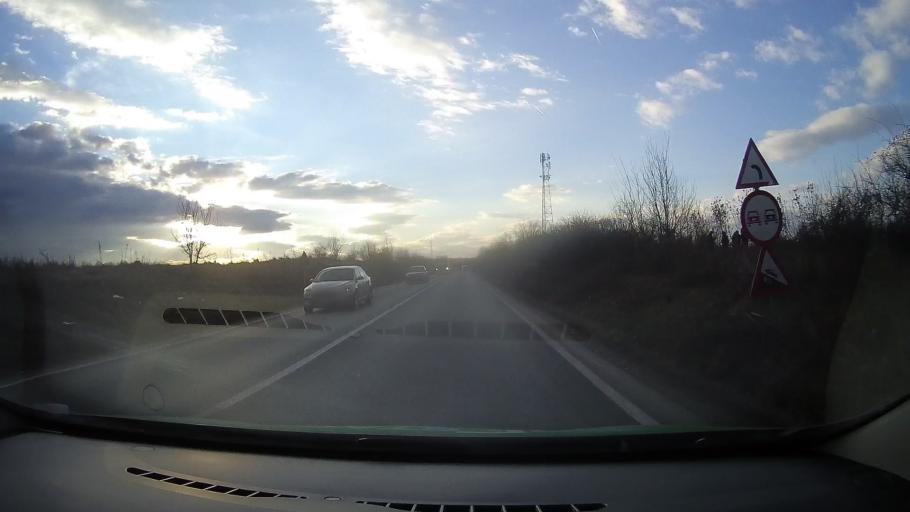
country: RO
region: Dambovita
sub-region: Comuna I. L. Caragiale
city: Mija
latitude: 44.9129
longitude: 25.6741
